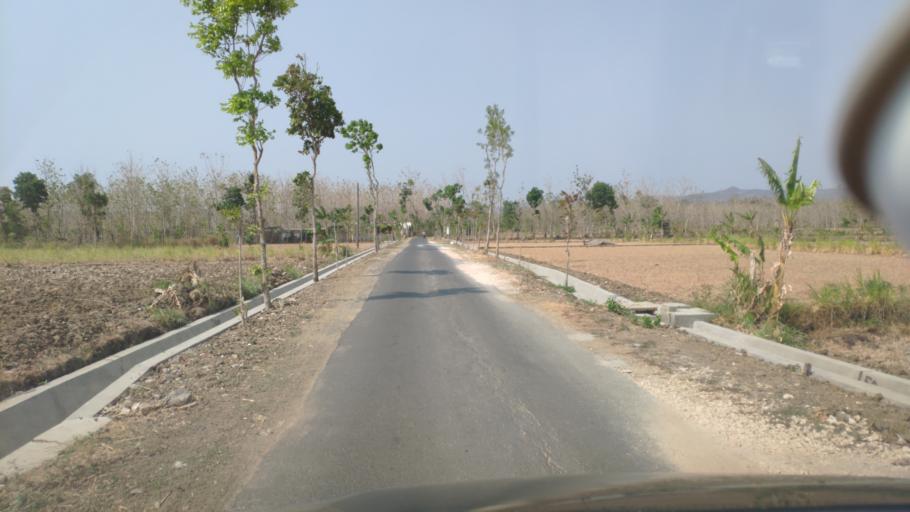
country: ID
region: Central Java
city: Karanggeneng
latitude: -6.9189
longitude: 111.4525
